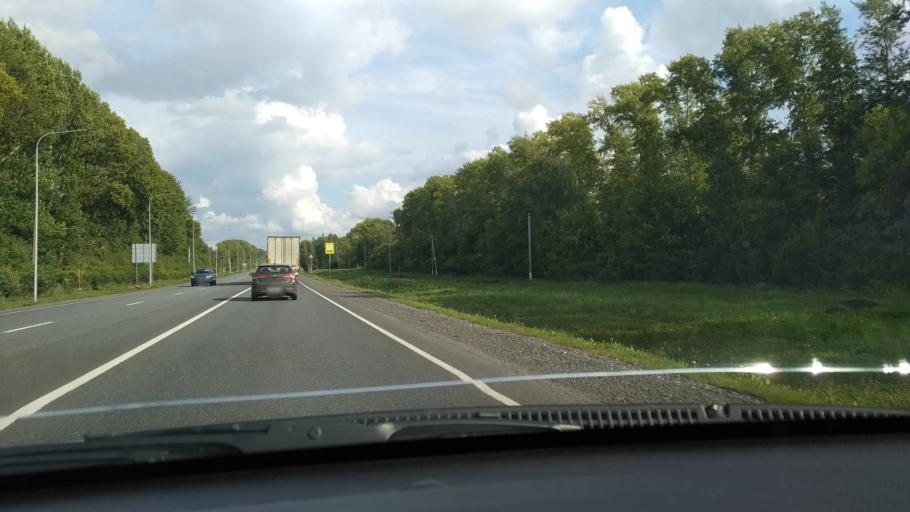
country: RU
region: Tatarstan
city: Stolbishchi
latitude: 55.6541
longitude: 49.3163
